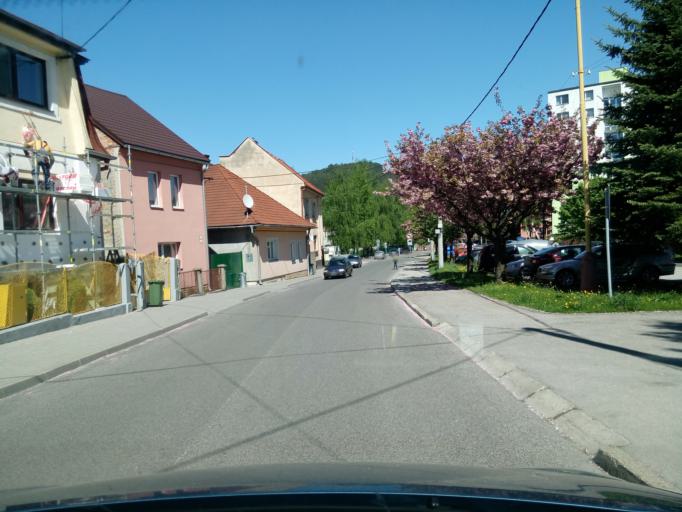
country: SK
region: Zilinsky
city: Ruzomberok
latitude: 49.0786
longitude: 19.3011
